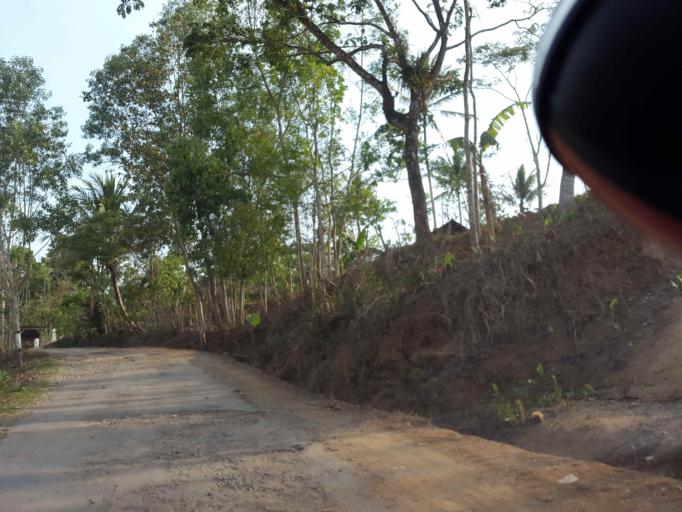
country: ID
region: East Java
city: Ploso
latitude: -8.0870
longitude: 111.0610
